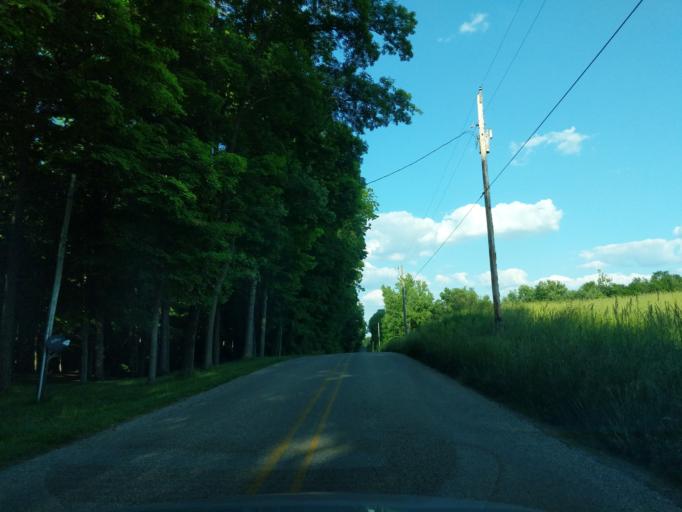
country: US
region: Indiana
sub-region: Kosciusko County
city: North Webster
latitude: 41.3026
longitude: -85.5698
